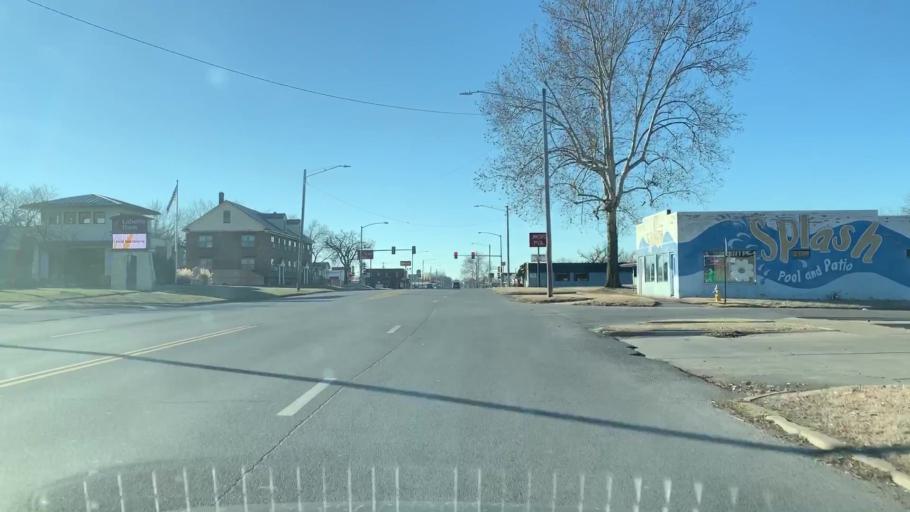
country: US
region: Kansas
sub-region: Crawford County
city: Pittsburg
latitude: 37.4015
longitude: -94.7050
